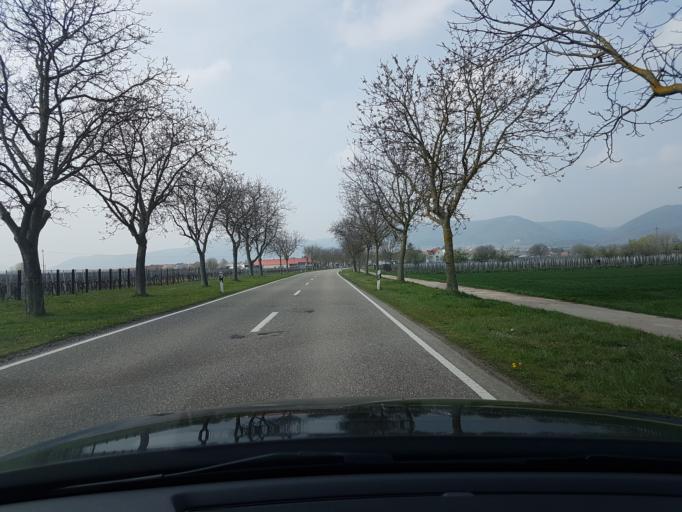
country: DE
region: Rheinland-Pfalz
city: Edesheim
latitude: 49.2634
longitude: 8.1486
